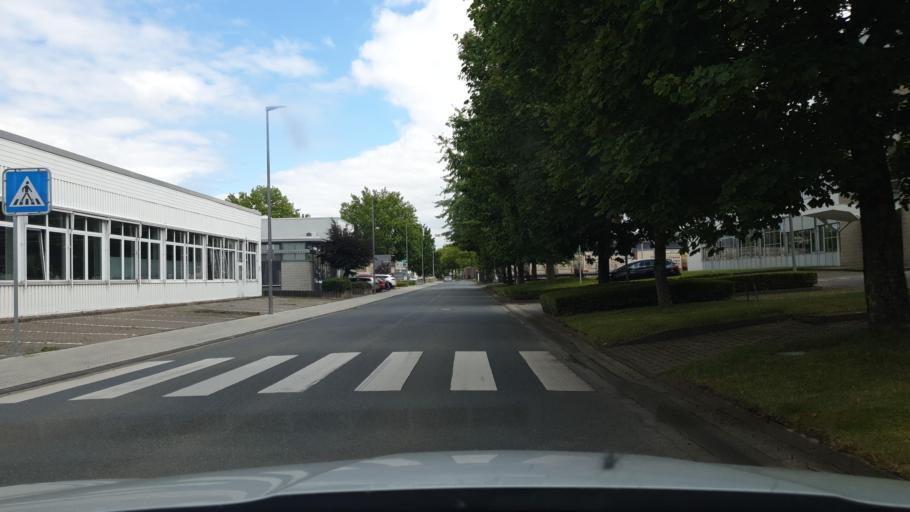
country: DE
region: North Rhine-Westphalia
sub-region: Regierungsbezirk Detmold
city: Lemgo
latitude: 52.0245
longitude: 8.8782
